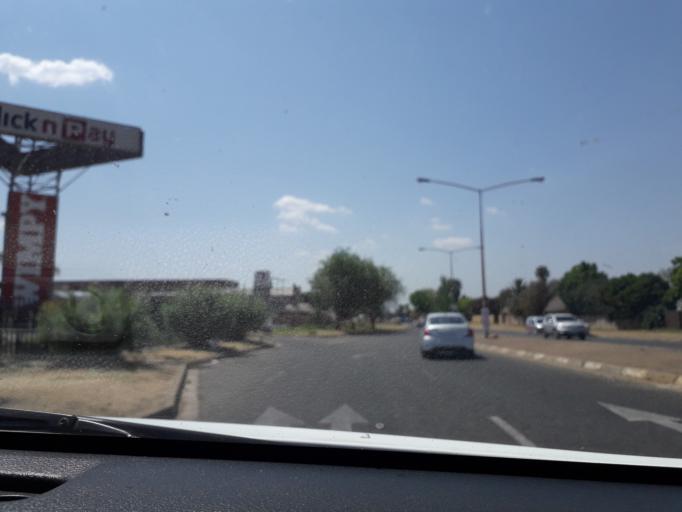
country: ZA
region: Gauteng
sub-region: City of Johannesburg Metropolitan Municipality
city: Modderfontein
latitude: -26.0946
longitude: 28.1978
